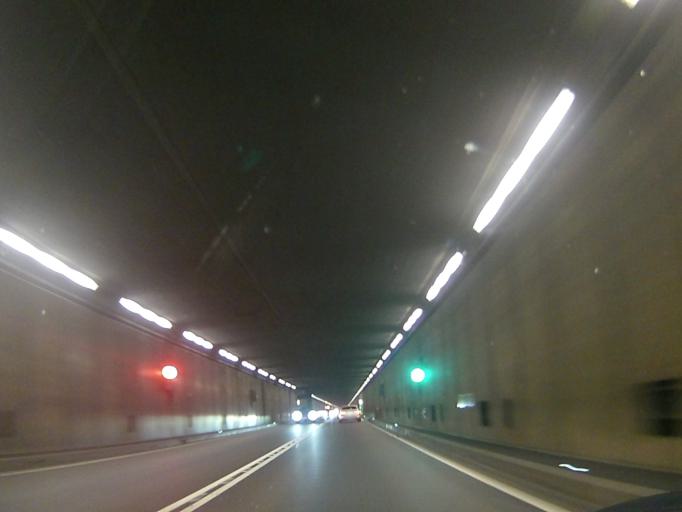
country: CH
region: Ticino
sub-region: Leventina District
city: Airolo
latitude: 46.5704
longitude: 8.5745
